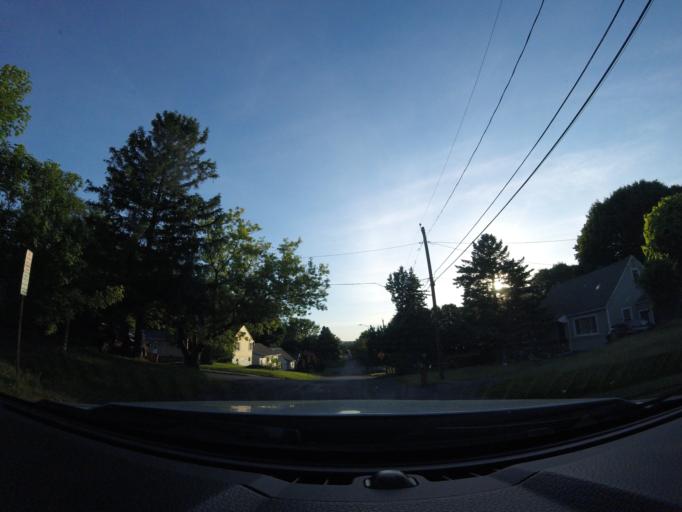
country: US
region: New York
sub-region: Onondaga County
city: Lyncourt
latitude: 43.0504
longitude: -76.1104
